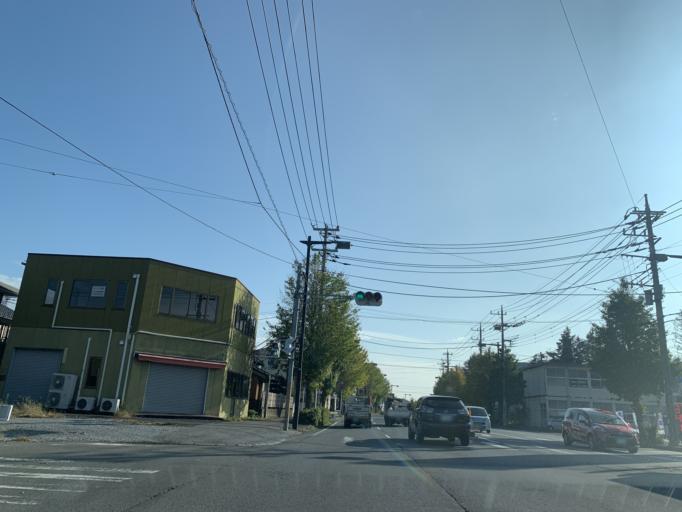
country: JP
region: Chiba
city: Nagareyama
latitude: 35.8630
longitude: 139.9119
